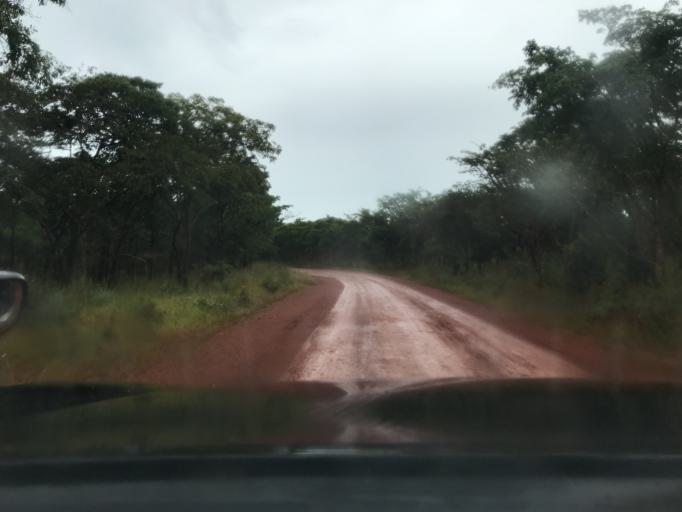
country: TZ
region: Kigoma
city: Uvinza
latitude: -5.2935
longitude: 30.3695
